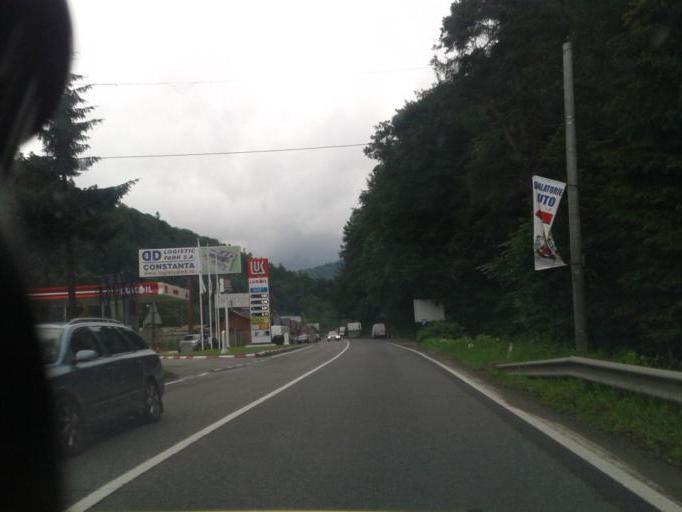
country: RO
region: Prahova
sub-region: Oras Azuga
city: Azuga
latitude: 45.4483
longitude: 25.5570
